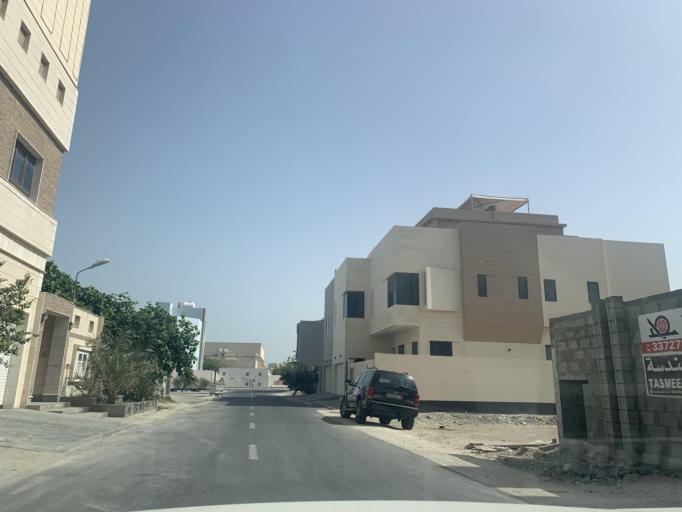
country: BH
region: Northern
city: Sitrah
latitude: 26.1664
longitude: 50.6284
